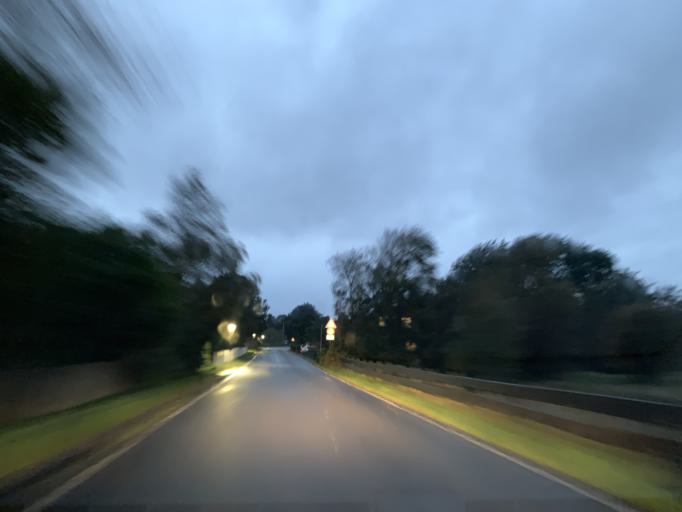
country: DE
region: Schleswig-Holstein
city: Nebel
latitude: 54.6409
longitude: 8.3608
